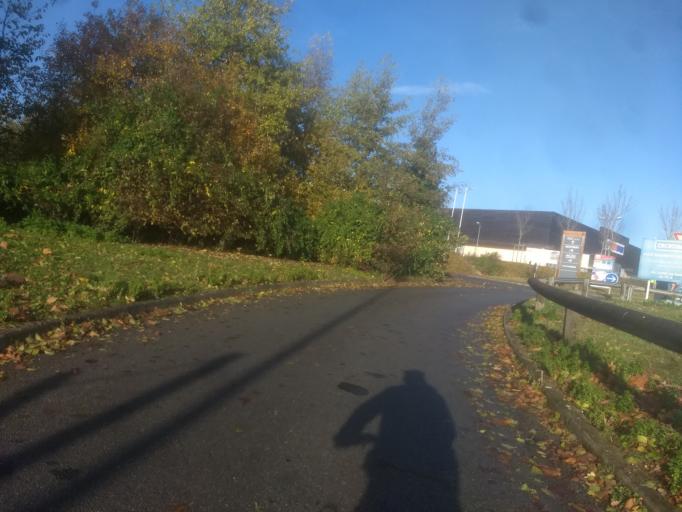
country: FR
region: Nord-Pas-de-Calais
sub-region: Departement du Pas-de-Calais
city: Anzin-Saint-Aubin
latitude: 50.3022
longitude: 2.7297
